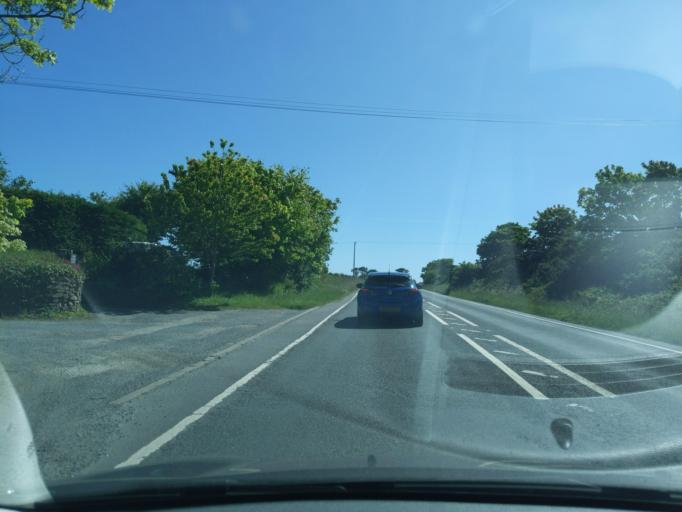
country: GB
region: England
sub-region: Cornwall
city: Wendron
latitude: 50.1469
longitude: -5.2117
